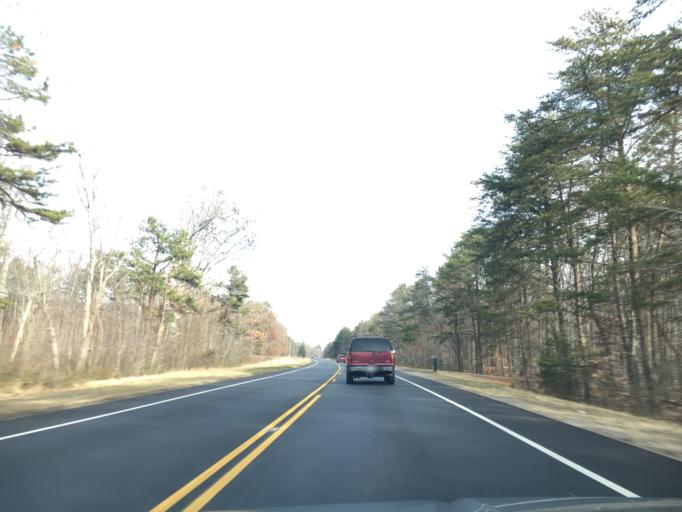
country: US
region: Virginia
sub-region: Louisa County
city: Louisa
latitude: 38.0257
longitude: -77.8978
